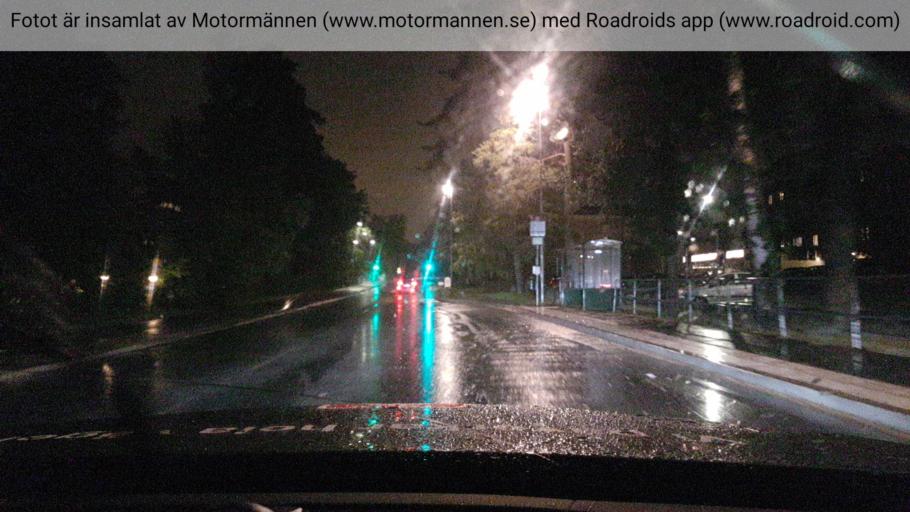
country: SE
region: Stockholm
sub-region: Haninge Kommun
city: Haninge
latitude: 59.1855
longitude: 18.1831
